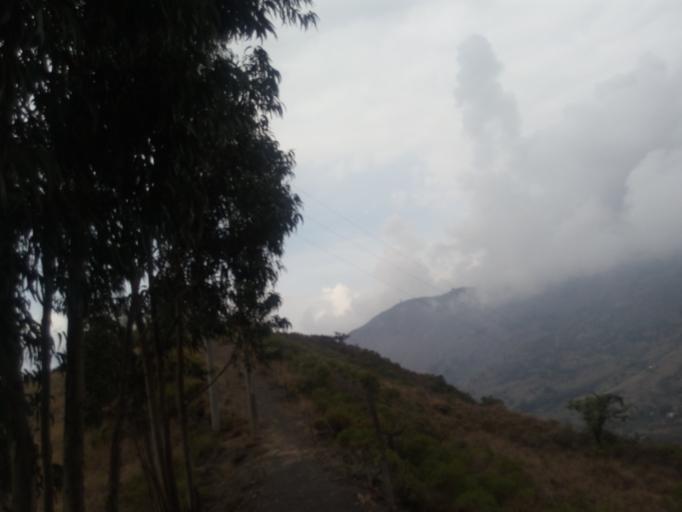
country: CO
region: Boyaca
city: Chita
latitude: 6.1919
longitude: -72.4936
